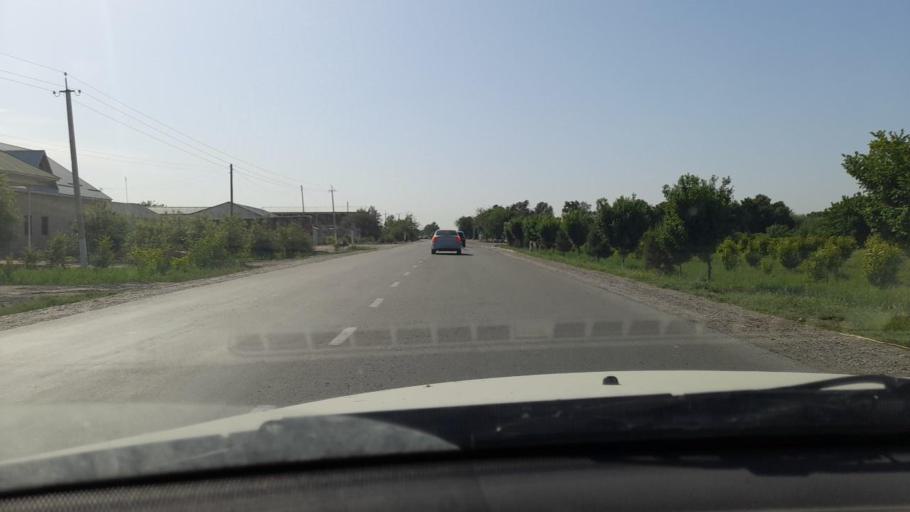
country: UZ
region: Bukhara
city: Galaosiyo
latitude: 39.8847
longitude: 64.4238
